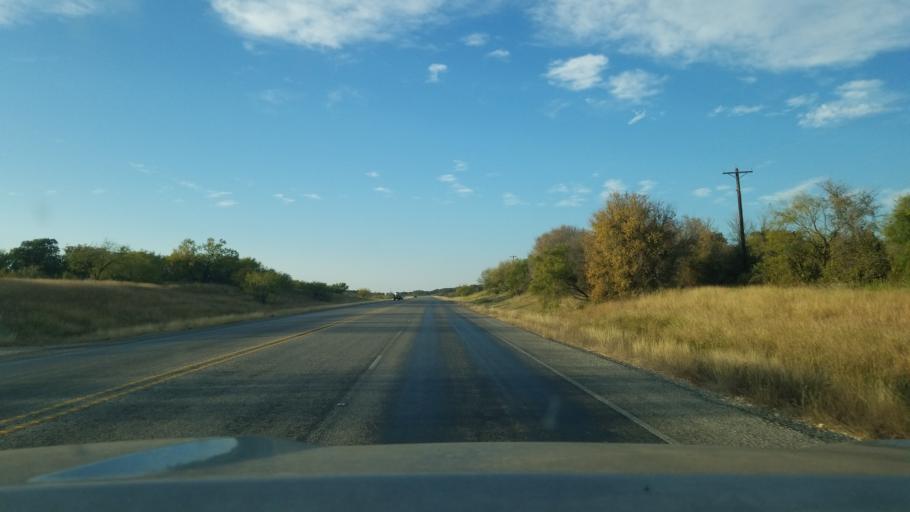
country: US
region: Texas
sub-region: Brown County
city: Lake Brownwood
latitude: 32.0567
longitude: -98.9464
